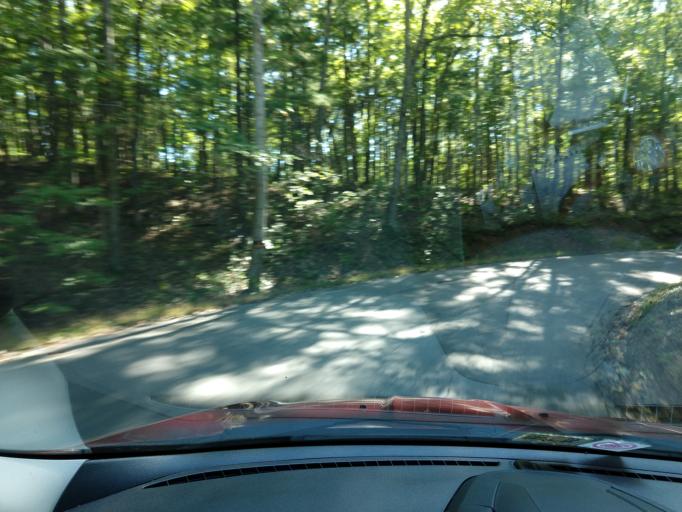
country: US
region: Virginia
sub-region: Alleghany County
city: Clifton Forge
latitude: 37.8471
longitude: -79.8468
